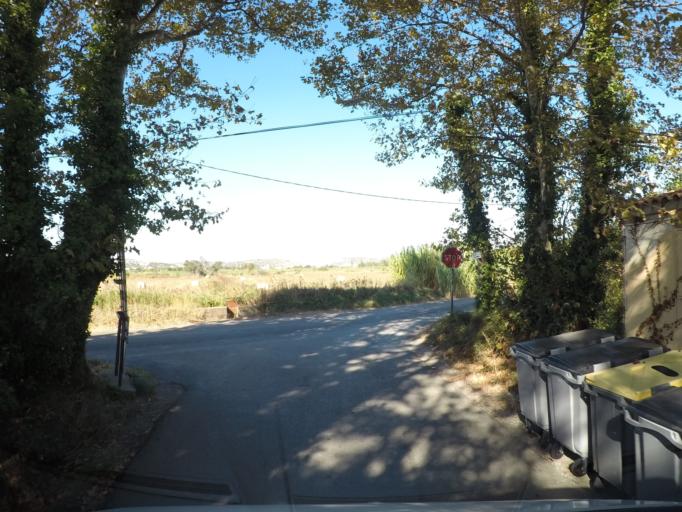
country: FR
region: Languedoc-Roussillon
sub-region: Departement de l'Aude
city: Narbonne
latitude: 43.1709
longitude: 3.0089
